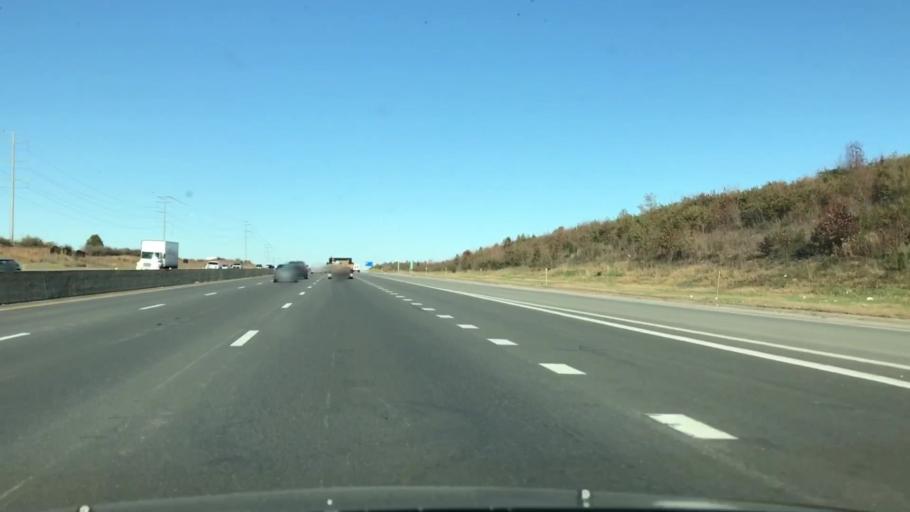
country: US
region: Missouri
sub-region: Jackson County
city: Grandview
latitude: 38.9556
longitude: -94.5279
